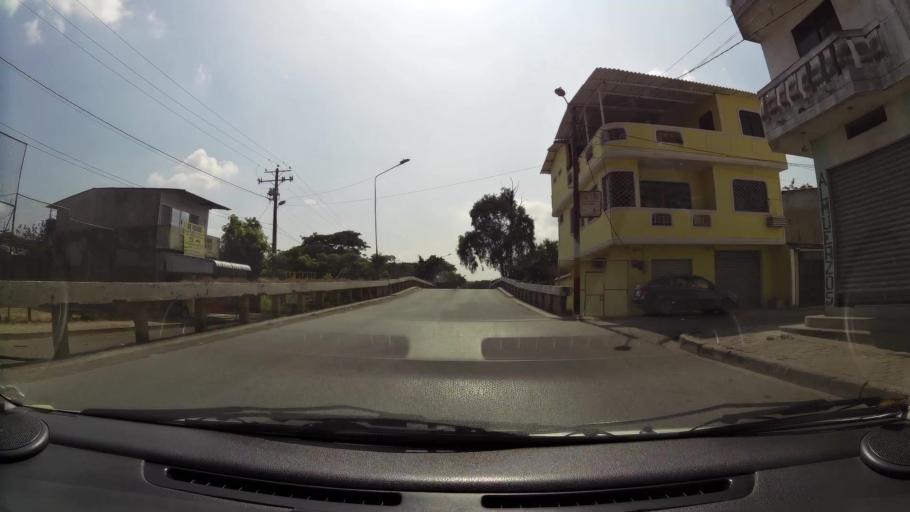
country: EC
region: Guayas
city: Eloy Alfaro
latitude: -2.1531
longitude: -79.8346
